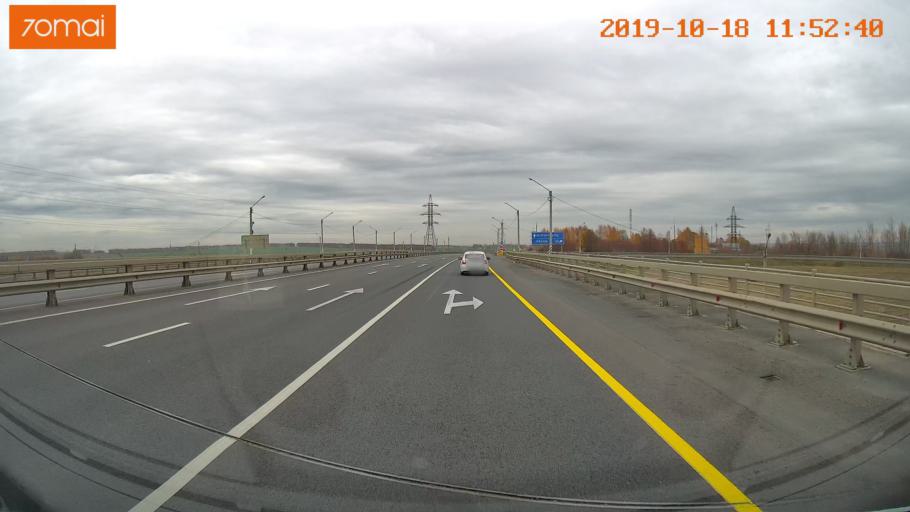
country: RU
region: Rjazan
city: Mikhaylov
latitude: 54.2462
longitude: 39.0531
